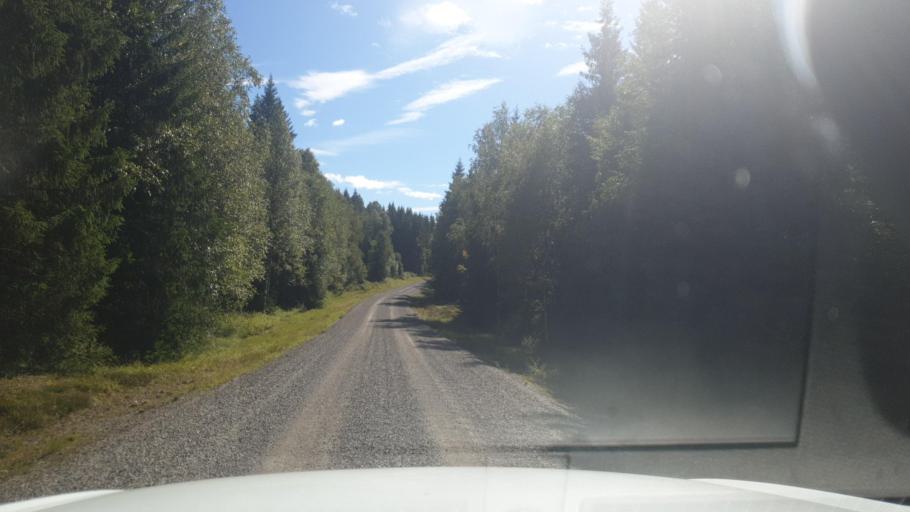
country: SE
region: Vaermland
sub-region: Eda Kommun
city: Charlottenberg
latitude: 60.1114
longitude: 12.6045
